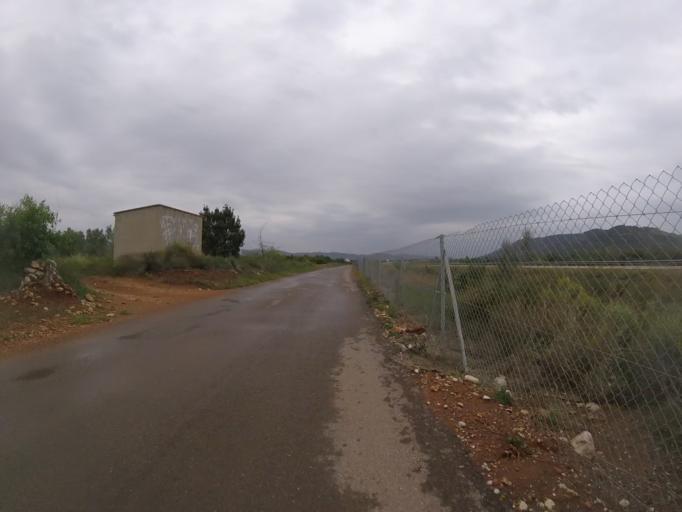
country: ES
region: Valencia
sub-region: Provincia de Castello
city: Alcala de Xivert
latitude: 40.2894
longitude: 0.2281
